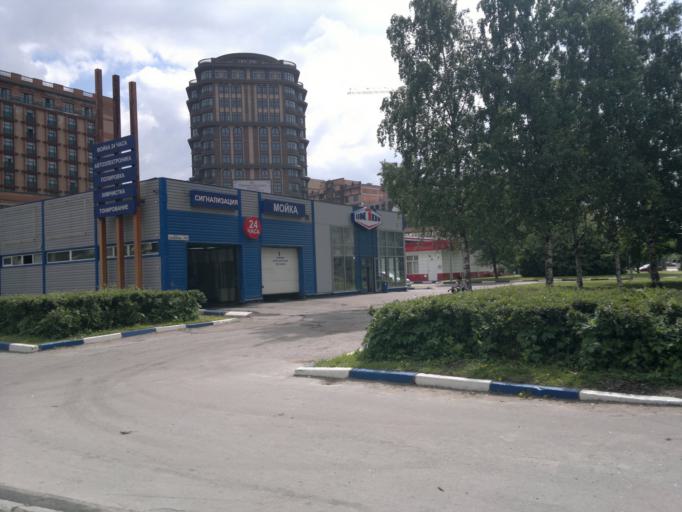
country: RU
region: St.-Petersburg
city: Vasyl'evsky Ostrov
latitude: 59.9413
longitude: 30.2254
